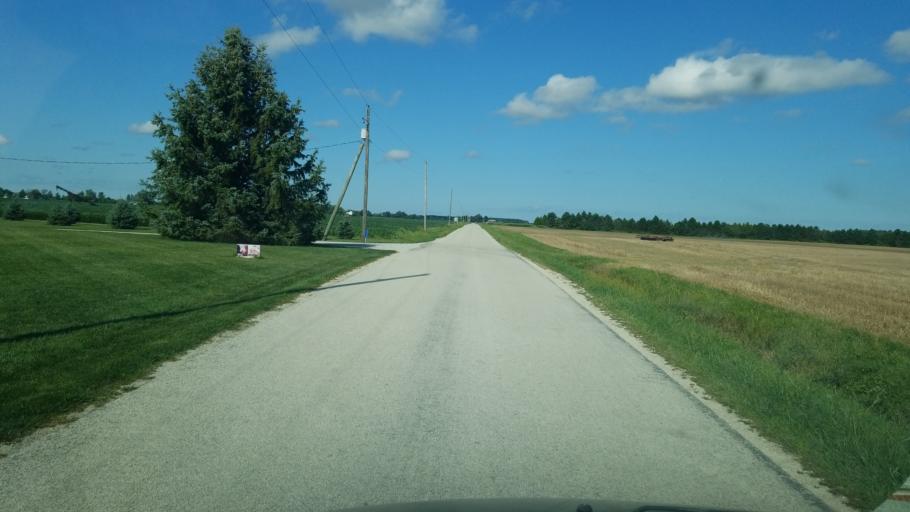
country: US
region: Ohio
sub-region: Seneca County
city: Fostoria
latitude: 41.0648
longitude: -83.4067
